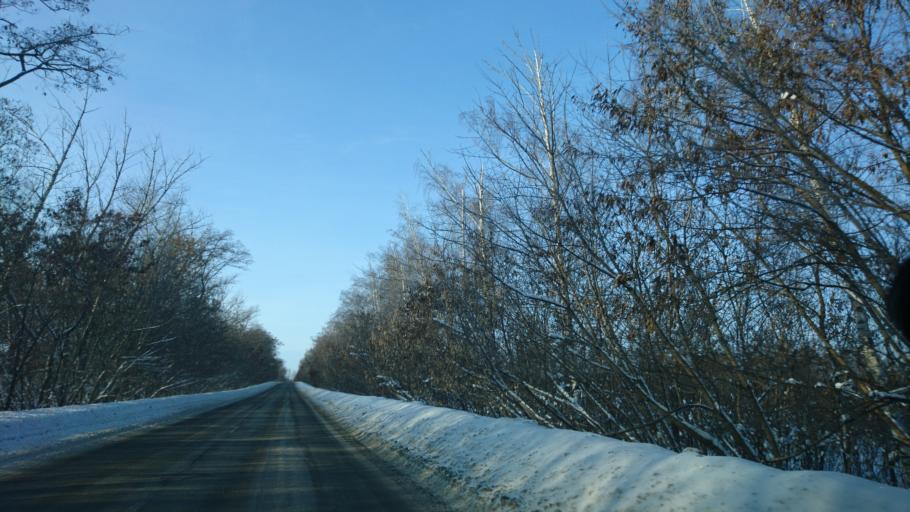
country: RU
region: Belgorod
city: Severnyy
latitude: 50.7266
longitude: 36.5709
